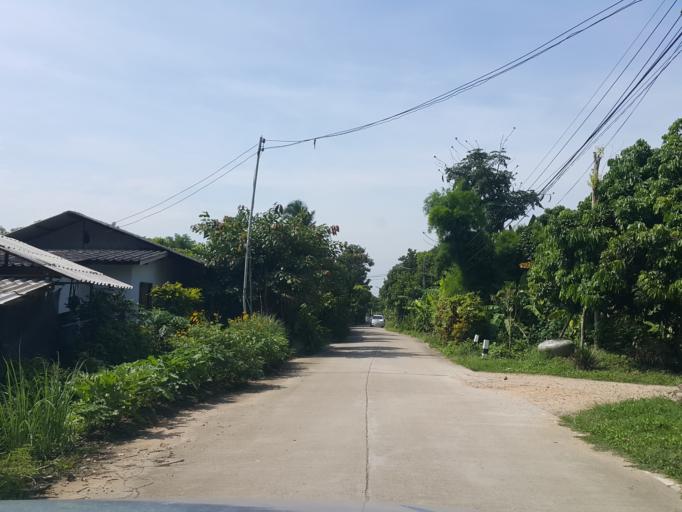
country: TH
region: Chiang Mai
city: Saraphi
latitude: 18.6914
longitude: 99.0703
